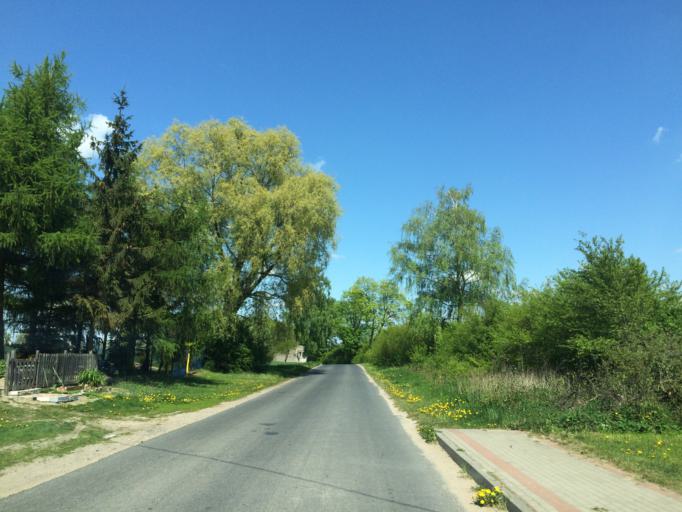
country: PL
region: Warmian-Masurian Voivodeship
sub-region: Powiat nowomiejski
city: Biskupiec
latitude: 53.4240
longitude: 19.2717
